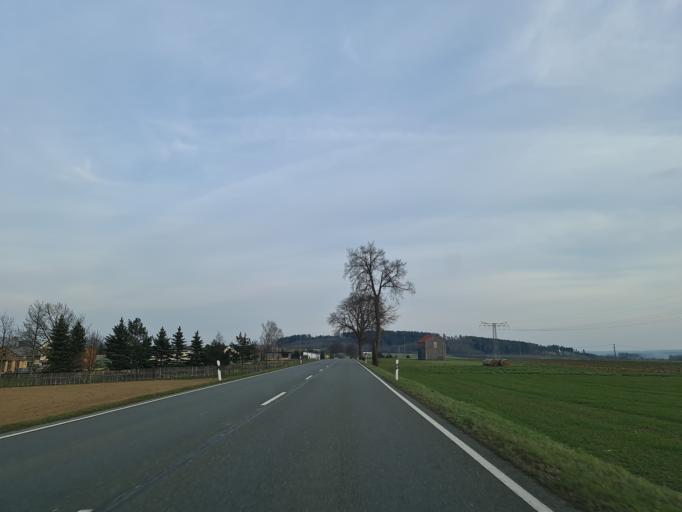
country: DE
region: Saxony
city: Plauen
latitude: 50.4592
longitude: 12.1581
